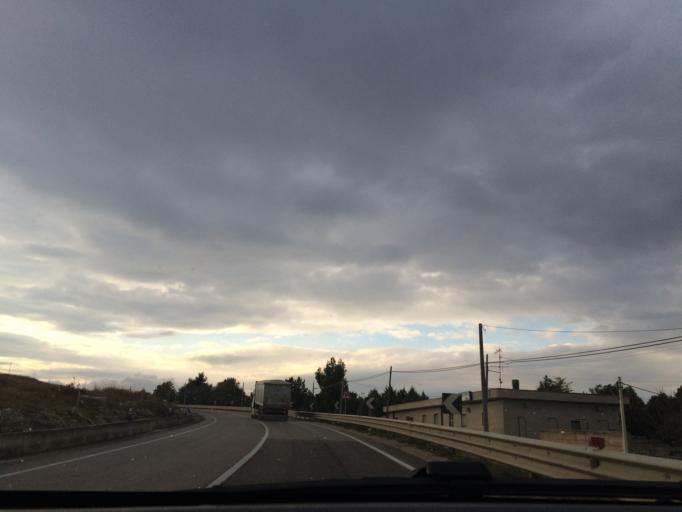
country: IT
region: Basilicate
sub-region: Provincia di Matera
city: Matera
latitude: 40.6794
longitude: 16.6269
